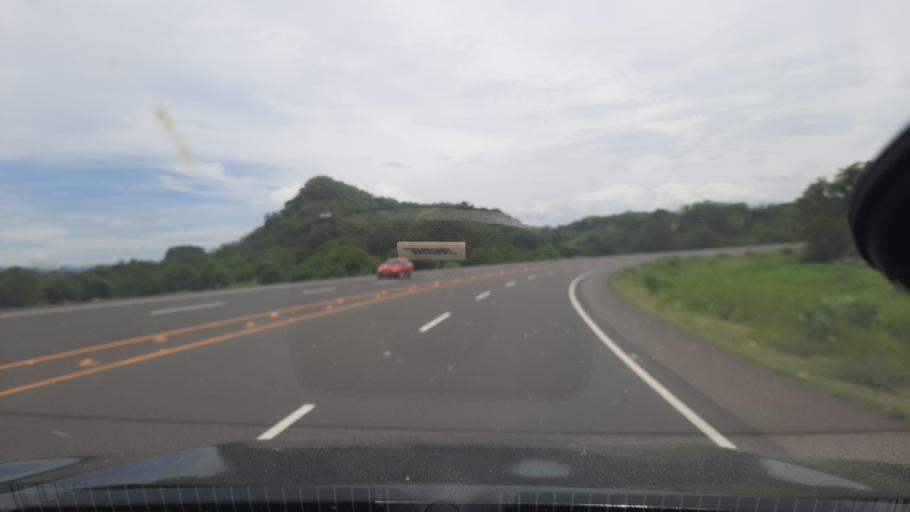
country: HN
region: Valle
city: Aramecina
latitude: 13.7170
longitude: -87.7093
